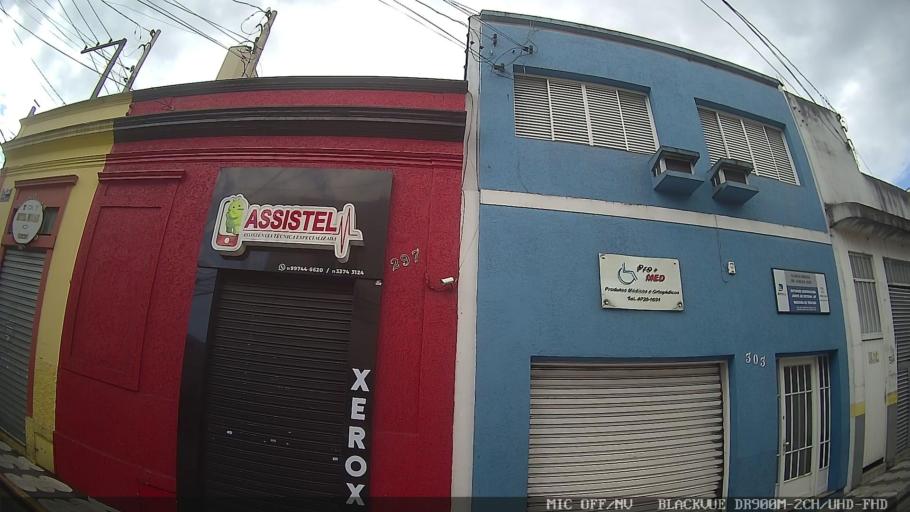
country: BR
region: Sao Paulo
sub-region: Mogi das Cruzes
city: Mogi das Cruzes
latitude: -23.5211
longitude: -46.1929
